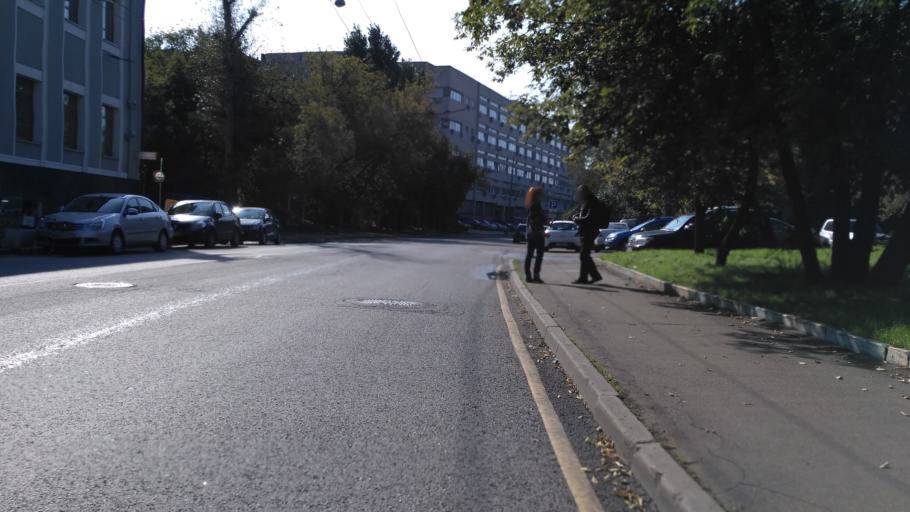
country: RU
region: Moscow
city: Lefortovo
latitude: 55.7662
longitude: 37.6748
